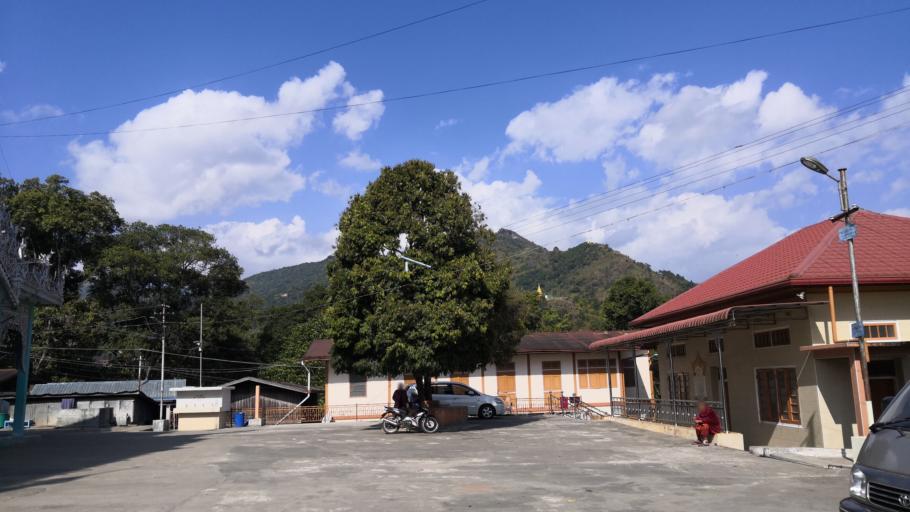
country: MM
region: Mandalay
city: Mogok
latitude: 22.9251
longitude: 96.5021
